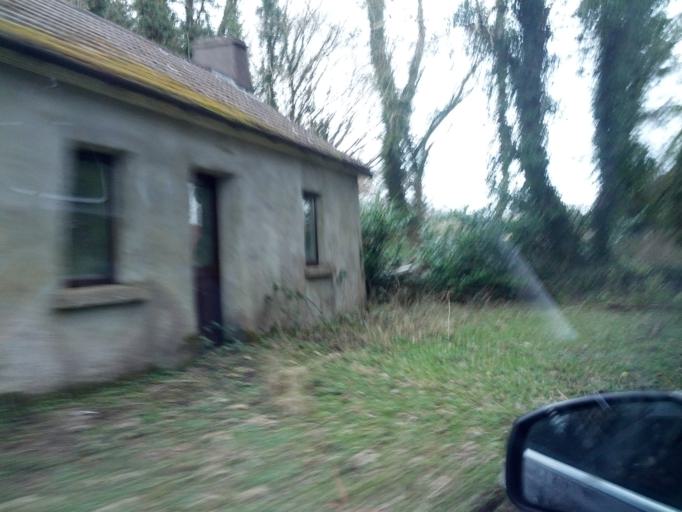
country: IE
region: Connaught
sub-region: County Galway
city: Athenry
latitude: 53.3865
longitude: -8.6305
